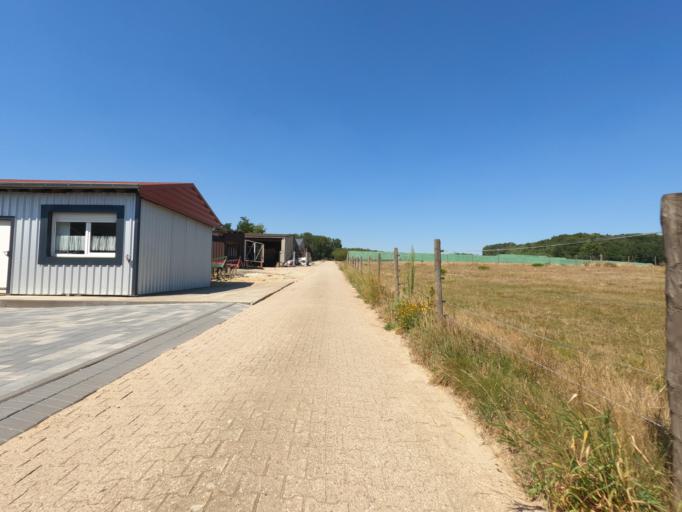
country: DE
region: North Rhine-Westphalia
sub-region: Regierungsbezirk Koln
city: Wassenberg
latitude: 51.0843
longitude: 6.1944
